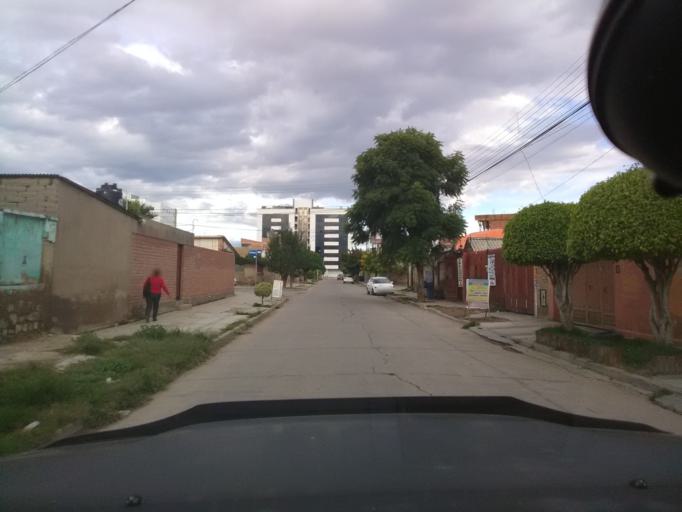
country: BO
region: Cochabamba
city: Cochabamba
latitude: -17.3781
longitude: -66.1876
